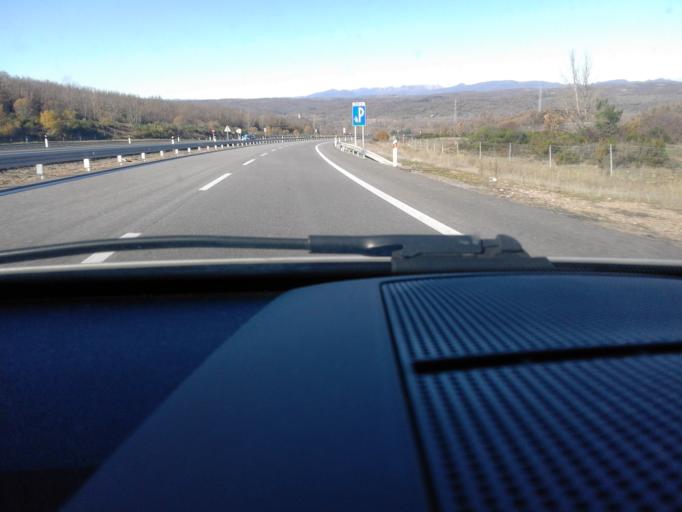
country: ES
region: Castille and Leon
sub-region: Provincia de Leon
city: Santa Maria de Ordas
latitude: 42.7067
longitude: -5.7913
